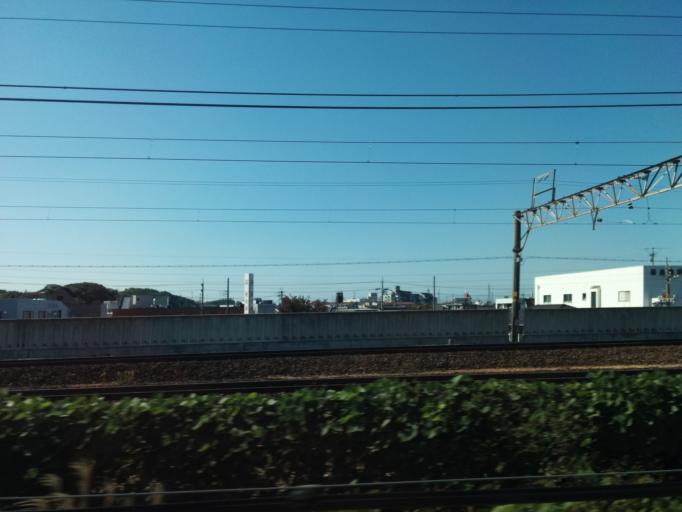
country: JP
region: Aichi
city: Obu
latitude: 35.0677
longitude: 136.9414
